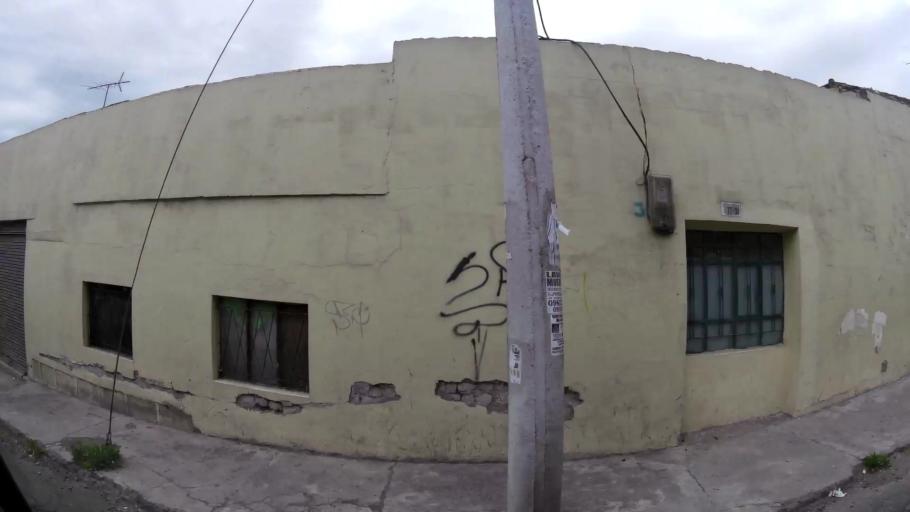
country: EC
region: Cotopaxi
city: Latacunga
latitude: -0.9330
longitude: -78.6258
